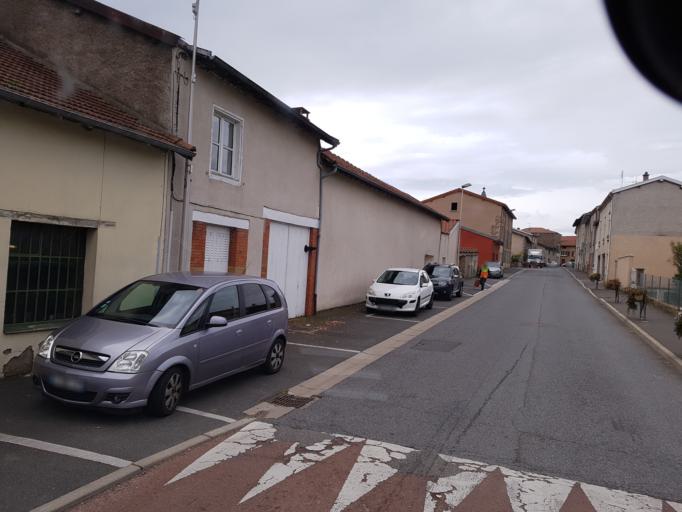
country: FR
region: Rhone-Alpes
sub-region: Departement de la Loire
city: Chazelles-sur-Lyon
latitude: 45.6569
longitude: 4.4214
